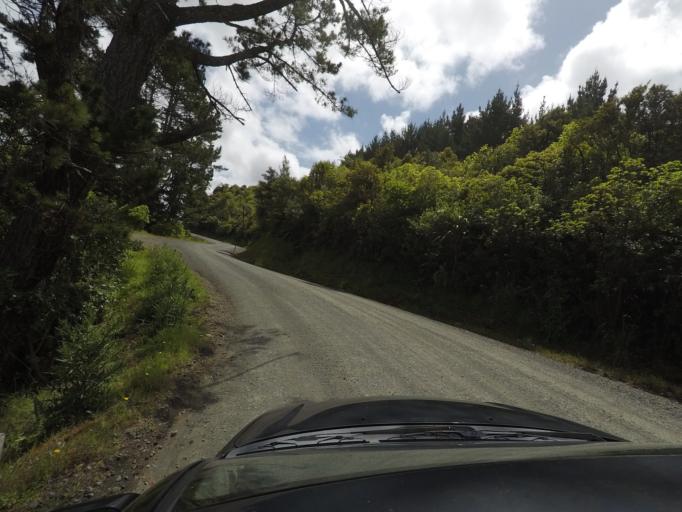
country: NZ
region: Auckland
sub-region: Auckland
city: Warkworth
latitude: -36.4829
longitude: 174.6043
